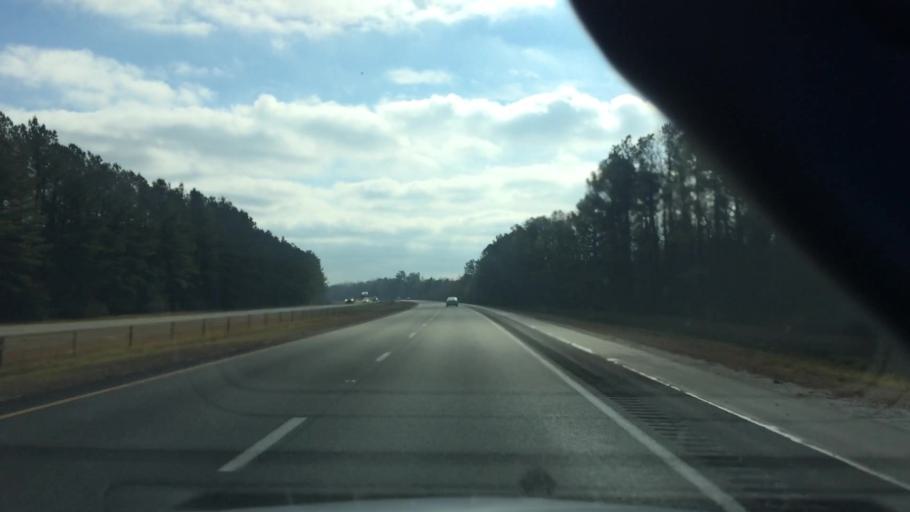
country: US
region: North Carolina
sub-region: Pender County
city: Rocky Point
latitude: 34.4678
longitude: -77.8801
